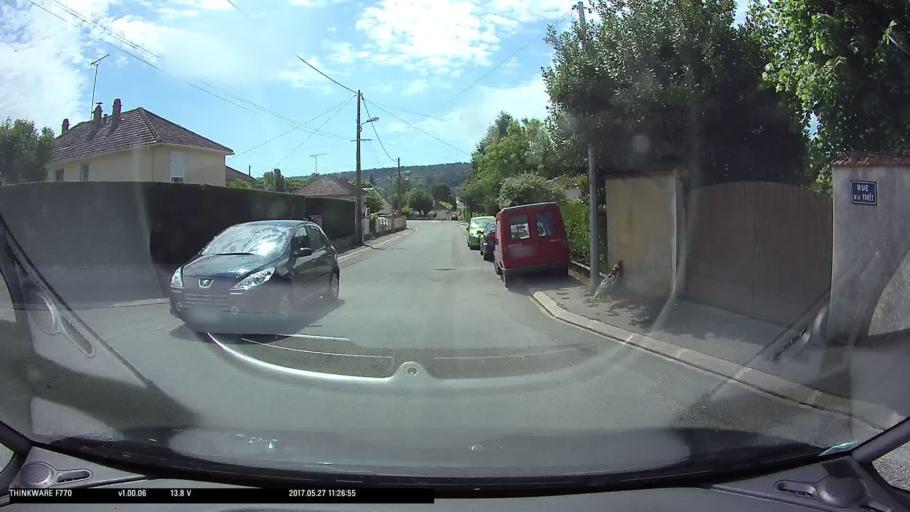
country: FR
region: Picardie
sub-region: Departement de l'Oise
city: Trie-Chateau
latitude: 49.2884
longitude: 1.8194
